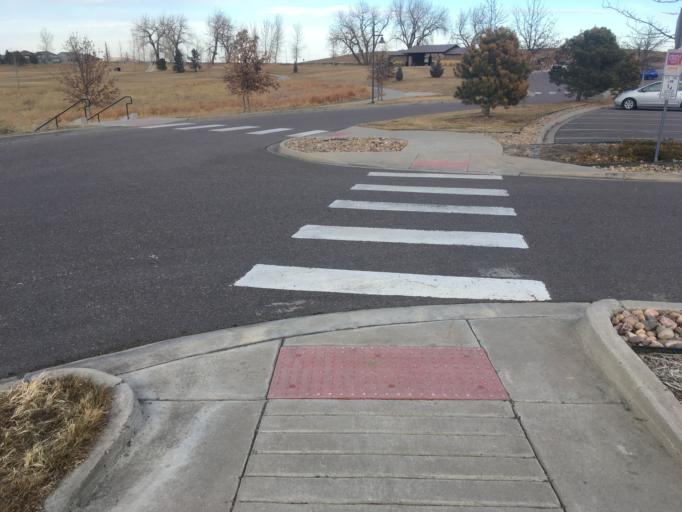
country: US
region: Colorado
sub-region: Boulder County
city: Lafayette
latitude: 39.9807
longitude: -105.0264
